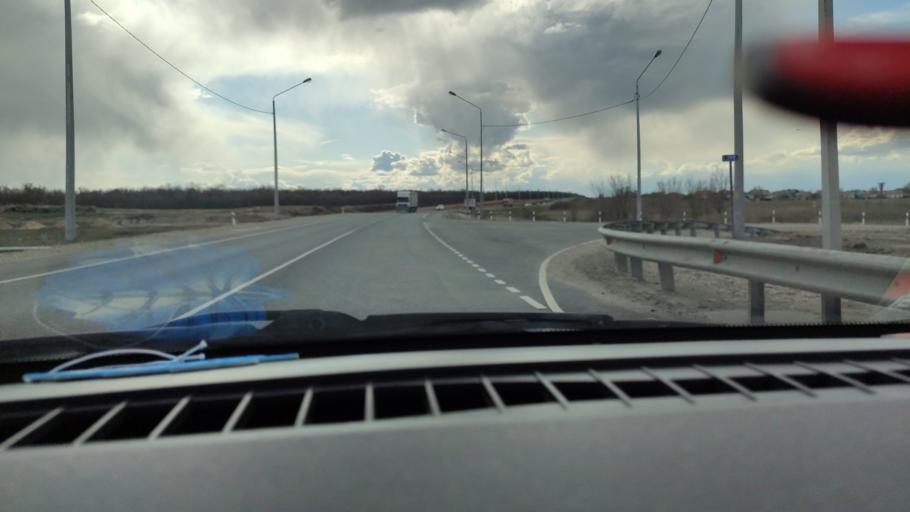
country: RU
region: Saratov
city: Sennoy
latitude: 52.1584
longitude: 47.0692
